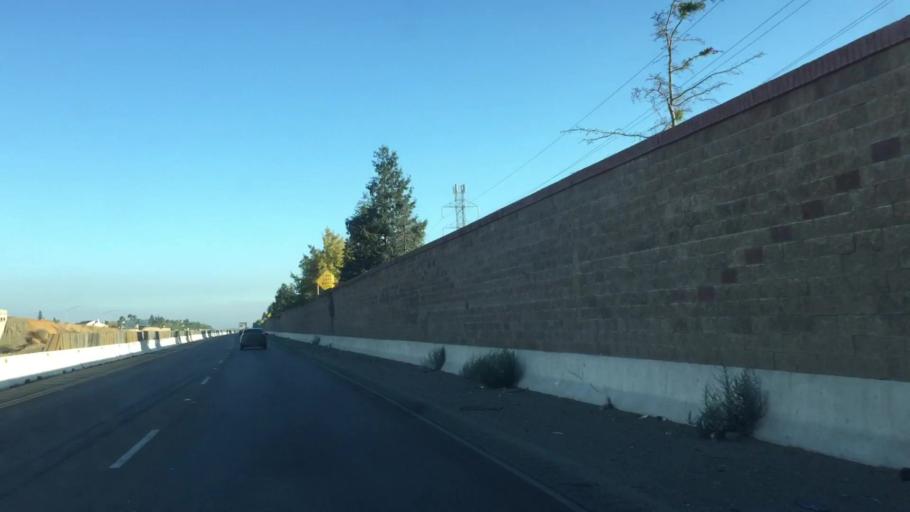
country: US
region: California
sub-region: Contra Costa County
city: Brentwood
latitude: 37.9262
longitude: -121.7330
